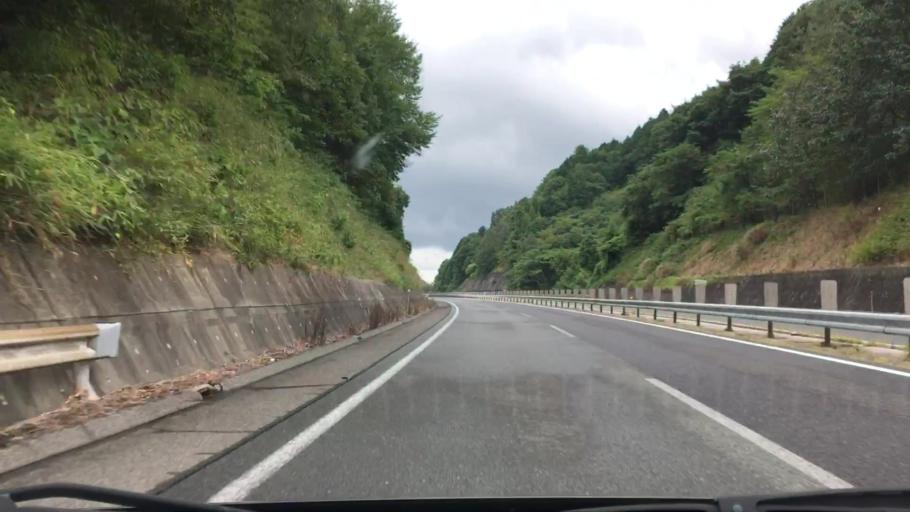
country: JP
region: Okayama
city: Niimi
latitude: 34.9395
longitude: 133.3279
